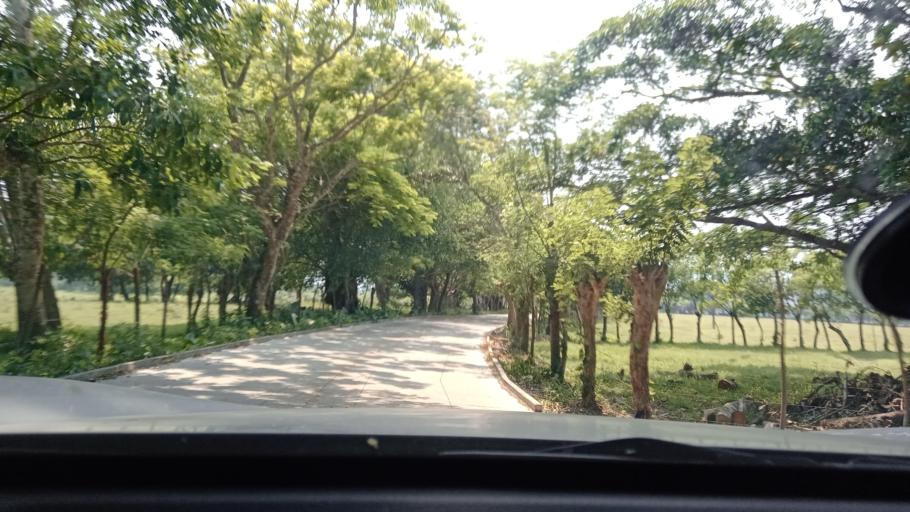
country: MX
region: Veracruz
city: Catemaco
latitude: 18.5606
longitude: -95.0337
